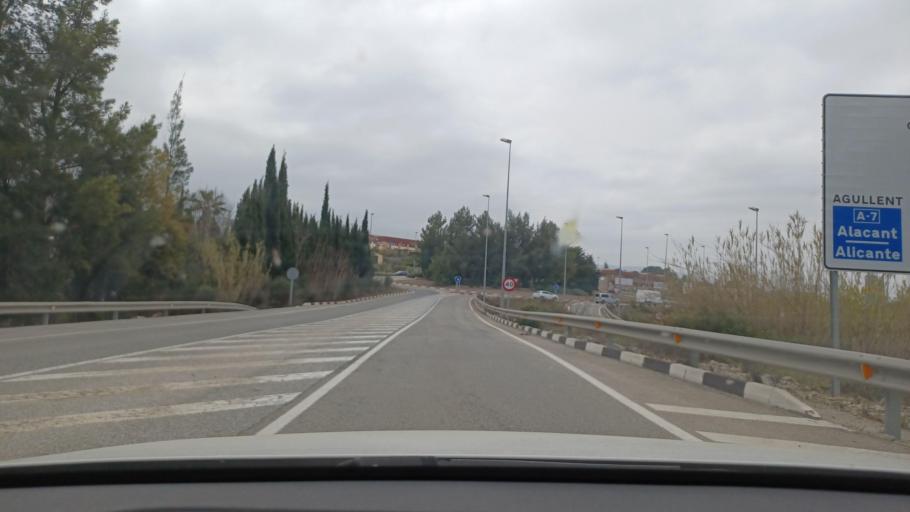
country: ES
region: Valencia
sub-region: Provincia de Valencia
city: Agullent
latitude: 38.8324
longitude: -0.5651
